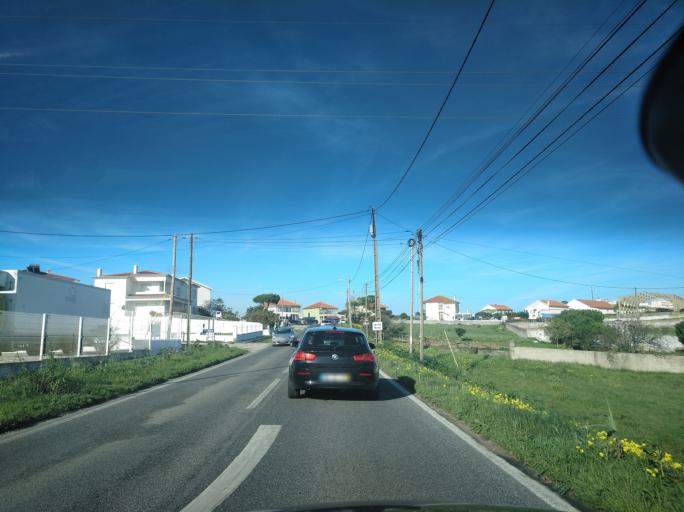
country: PT
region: Lisbon
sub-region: Mafra
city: Mafra
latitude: 38.9126
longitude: -9.3274
